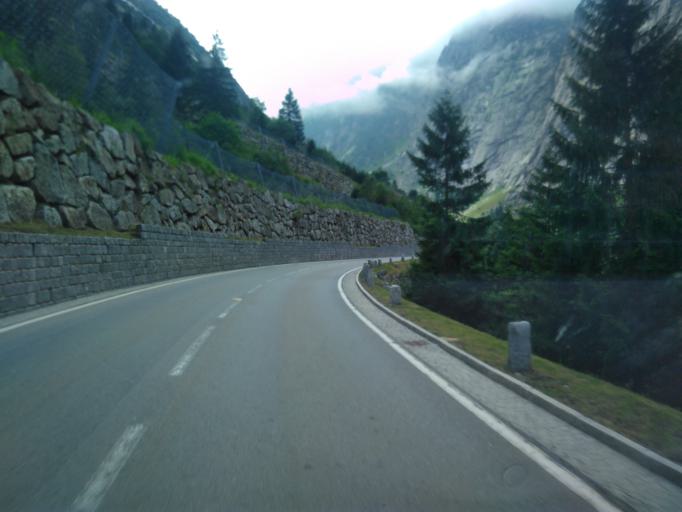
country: CH
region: Uri
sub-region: Uri
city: Andermatt
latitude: 46.6629
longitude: 8.5898
